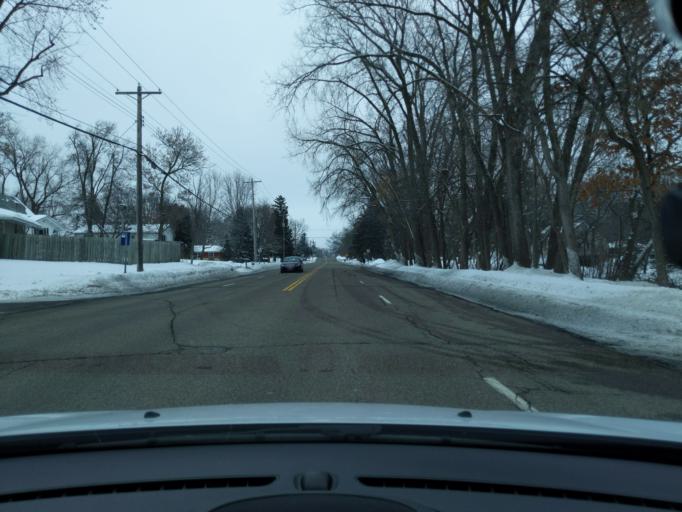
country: US
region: Minnesota
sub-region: Ramsey County
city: Little Canada
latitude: 45.0207
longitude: -93.1114
